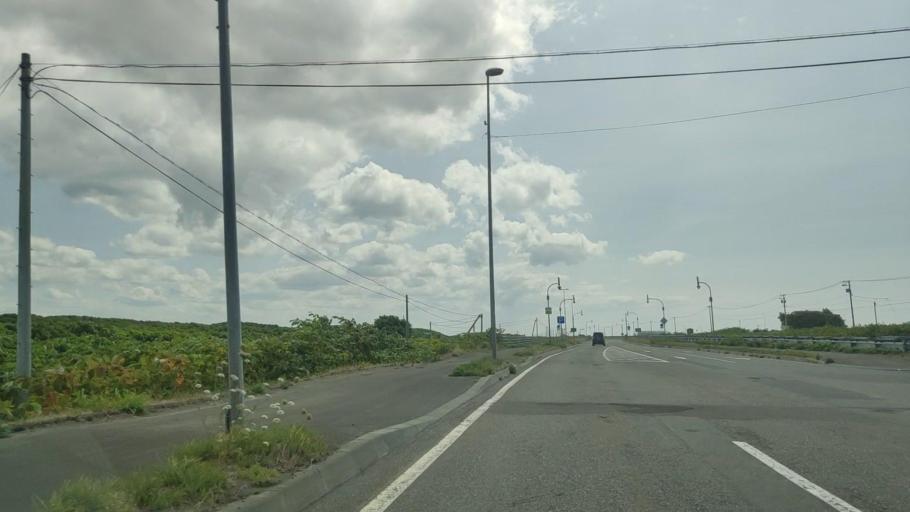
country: JP
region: Hokkaido
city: Makubetsu
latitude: 44.8727
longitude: 141.7517
